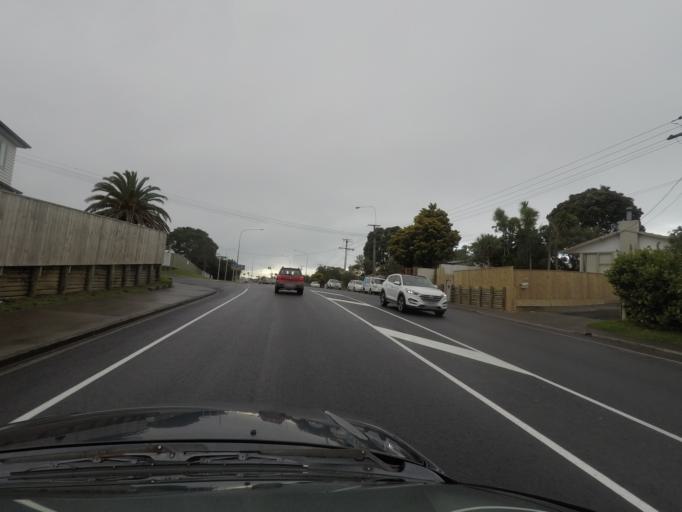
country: NZ
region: Auckland
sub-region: Auckland
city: Rothesay Bay
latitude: -36.7287
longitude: 174.7267
